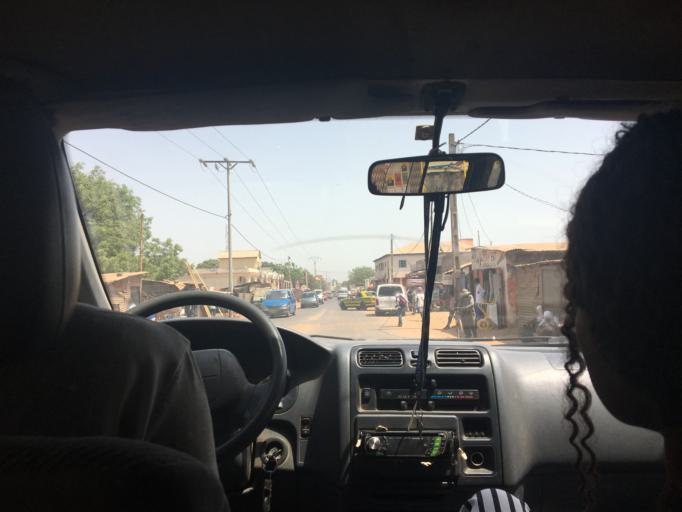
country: GM
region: Western
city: Abuko
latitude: 13.3911
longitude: -16.6751
